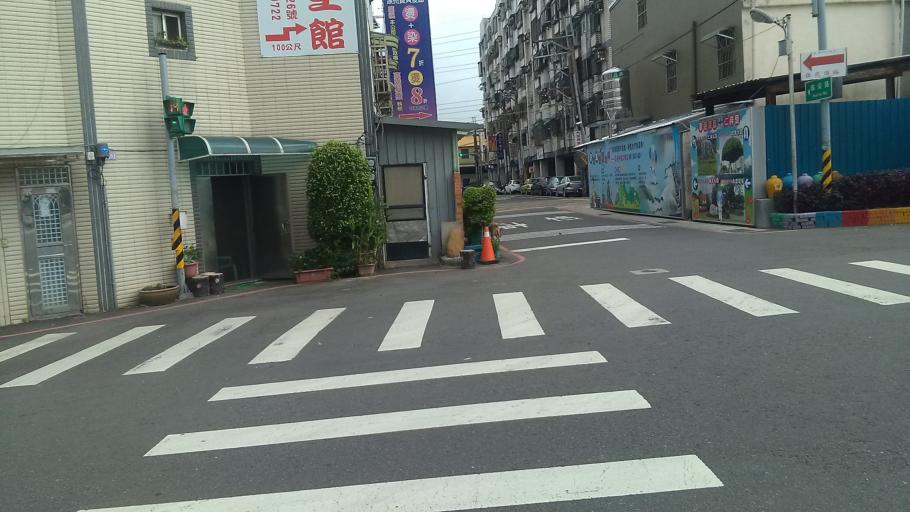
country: TW
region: Taiwan
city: Taoyuan City
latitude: 24.9508
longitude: 121.2616
